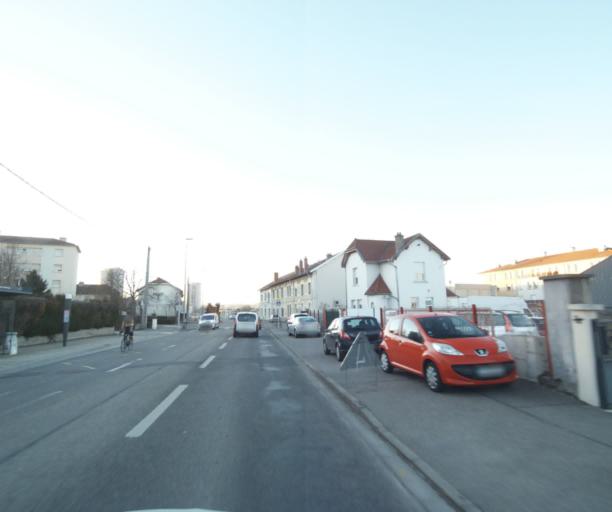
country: FR
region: Lorraine
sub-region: Departement de Meurthe-et-Moselle
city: Jarville-la-Malgrange
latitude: 48.6653
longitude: 6.2166
